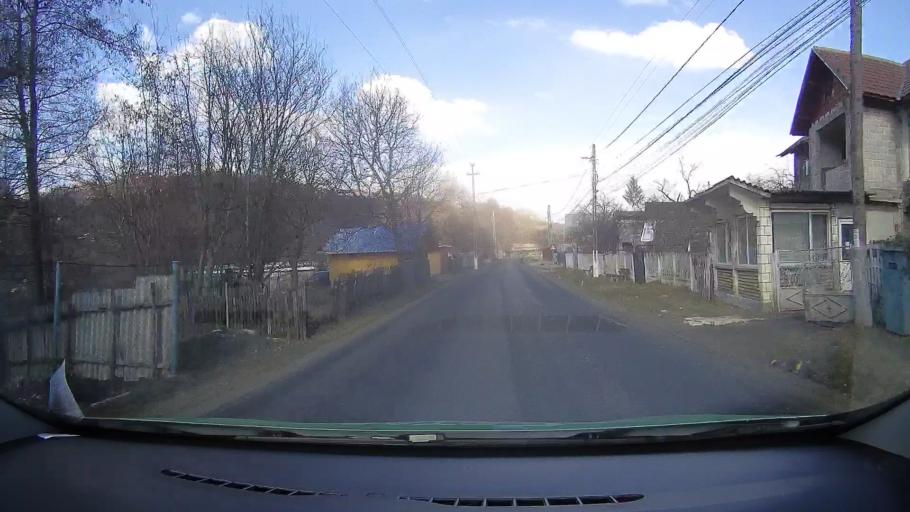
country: RO
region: Dambovita
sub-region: Comuna Runcu
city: Badeni
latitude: 45.1560
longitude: 25.3993
